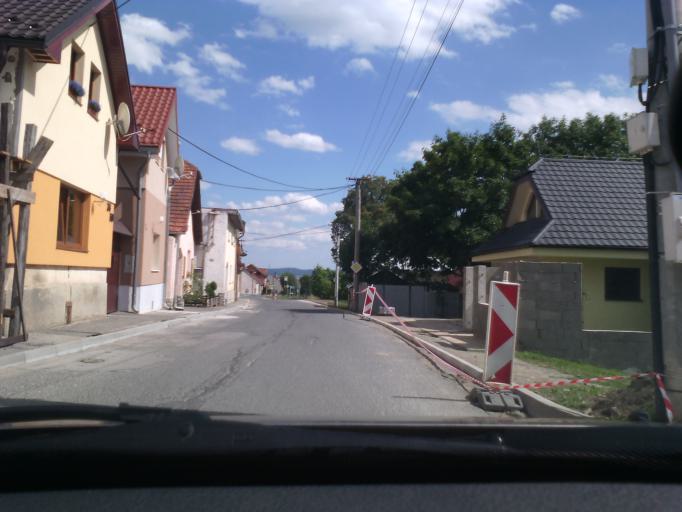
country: SK
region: Presovsky
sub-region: Okres Poprad
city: Nova Lesna
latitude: 49.1359
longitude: 20.3083
